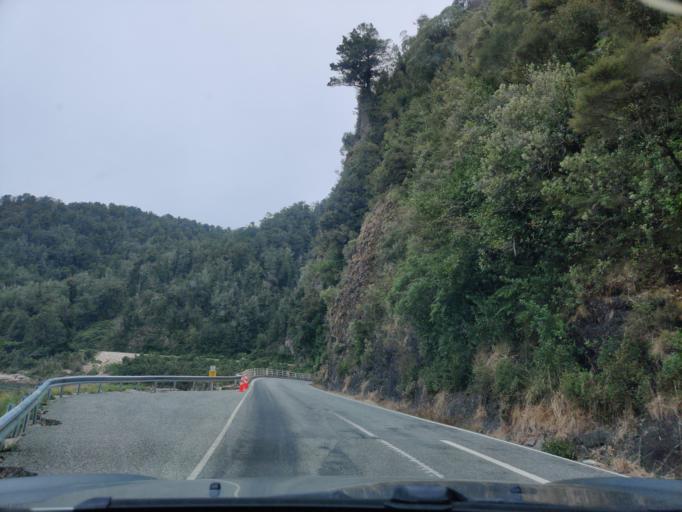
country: NZ
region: West Coast
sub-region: Buller District
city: Westport
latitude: -41.8645
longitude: 171.7783
